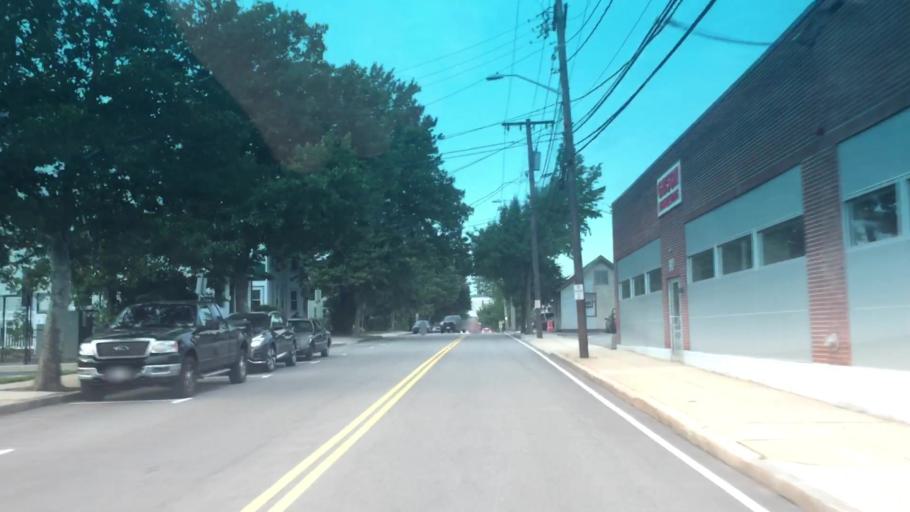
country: US
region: Massachusetts
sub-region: Norfolk County
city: Norwood
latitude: 42.1900
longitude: -71.1998
